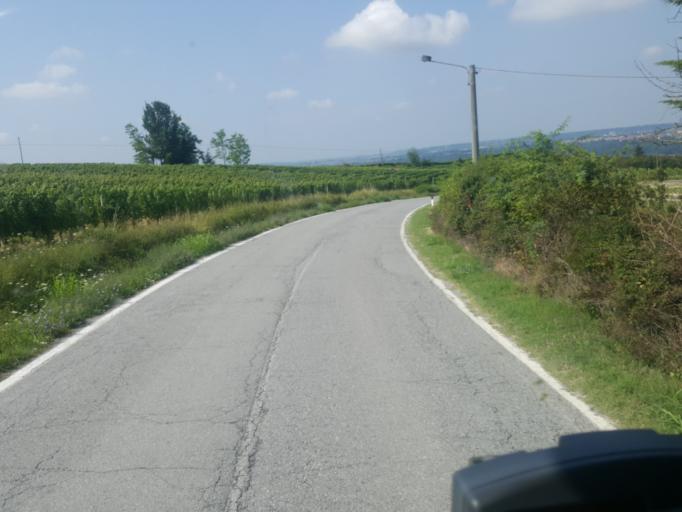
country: IT
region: Piedmont
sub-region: Provincia di Cuneo
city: Novello
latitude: 44.6075
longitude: 7.9158
